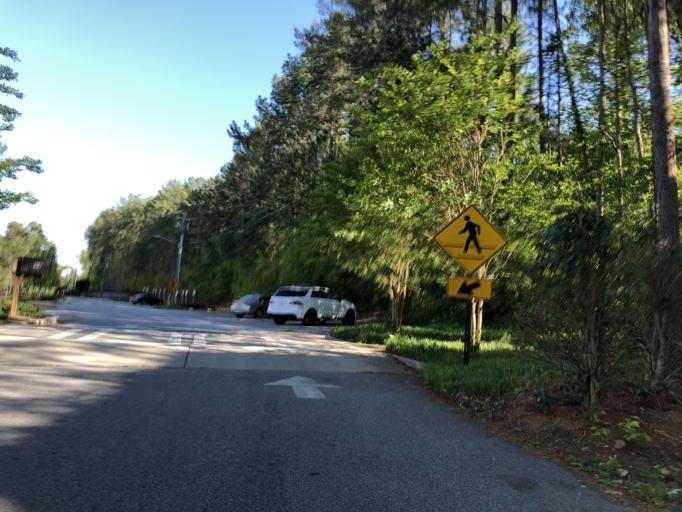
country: US
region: Georgia
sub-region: DeKalb County
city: North Druid Hills
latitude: 33.8078
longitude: -84.3078
